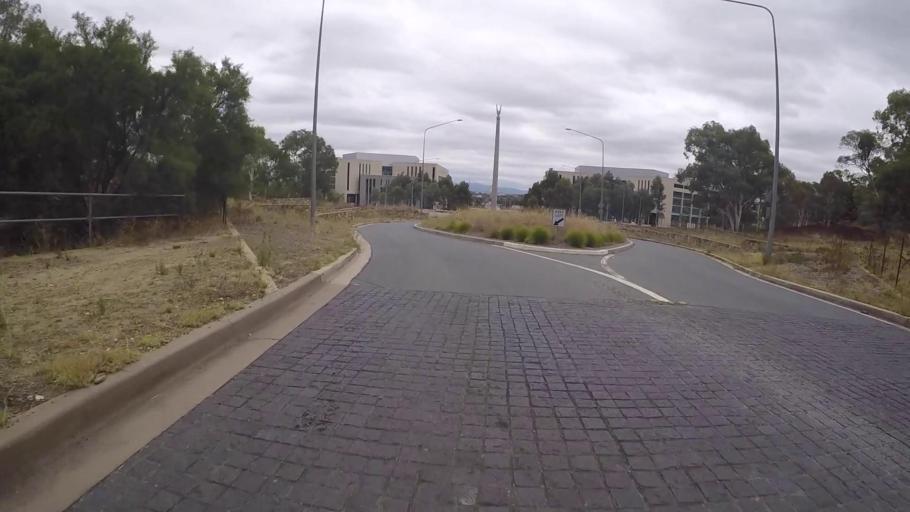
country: AU
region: Australian Capital Territory
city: Canberra
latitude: -35.2965
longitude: 149.1546
